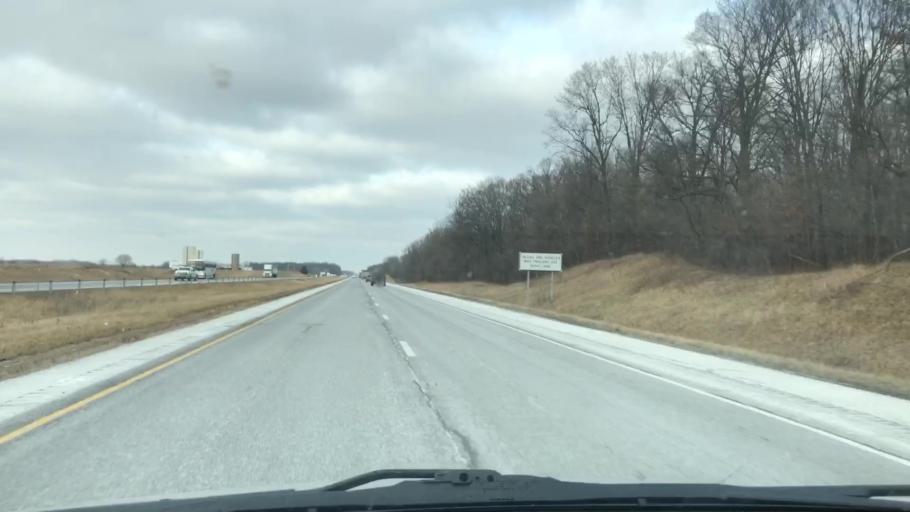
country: US
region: Indiana
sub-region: DeKalb County
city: Waterloo
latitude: 41.4497
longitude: -85.0537
